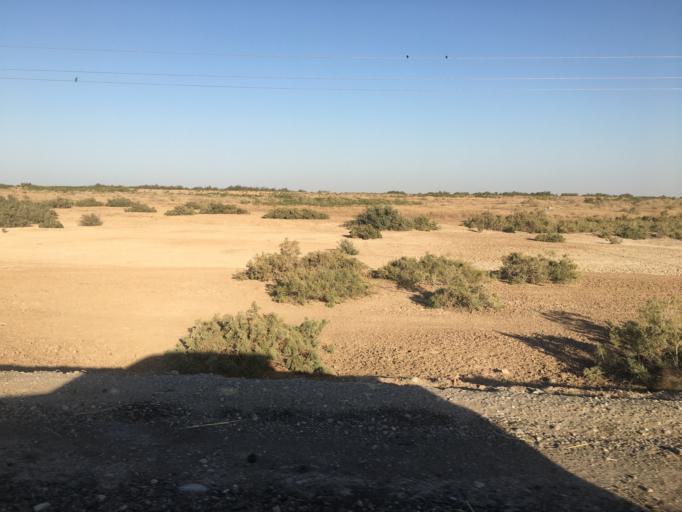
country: IR
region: Razavi Khorasan
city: Sarakhs
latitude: 37.1640
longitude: 61.2147
